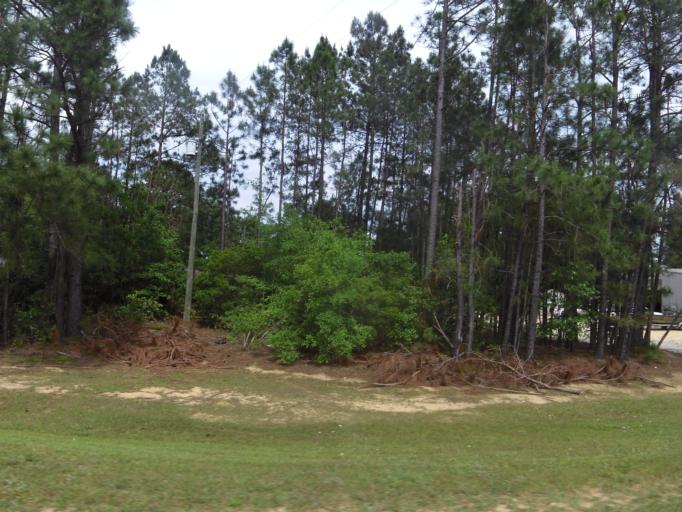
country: US
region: Georgia
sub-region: McDuffie County
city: Thomson
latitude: 33.3592
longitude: -82.4640
